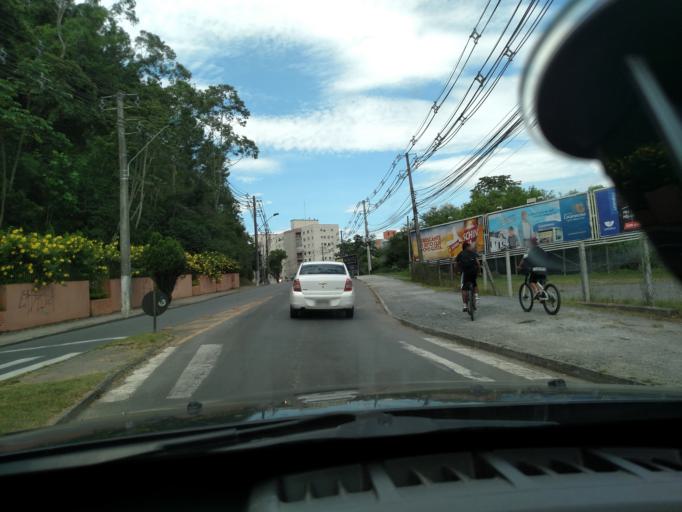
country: BR
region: Santa Catarina
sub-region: Blumenau
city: Blumenau
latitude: -26.9361
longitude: -49.0689
